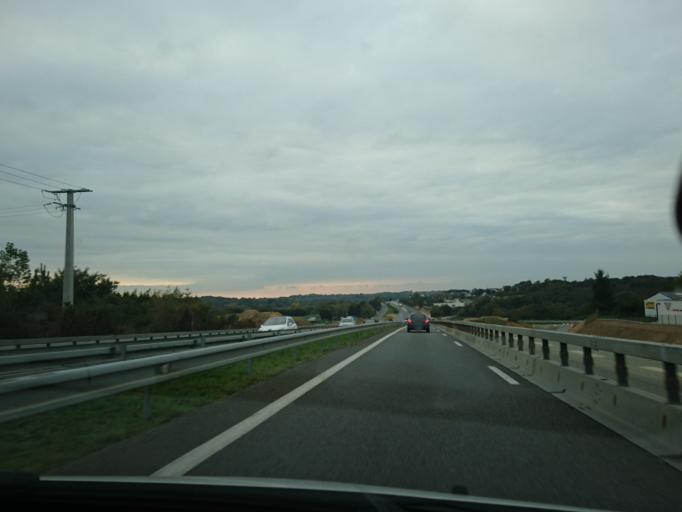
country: FR
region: Brittany
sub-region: Departement du Morbihan
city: Muzillac
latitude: 47.5494
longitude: -2.4615
